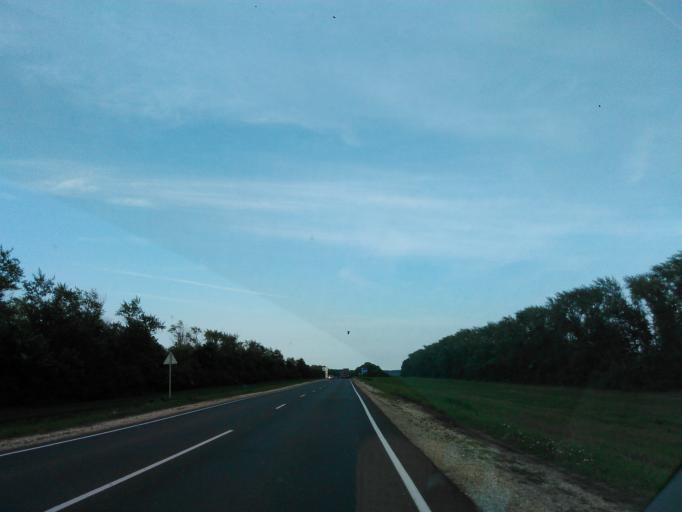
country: RU
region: Penza
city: Lermontovo
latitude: 52.9999
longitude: 43.6627
